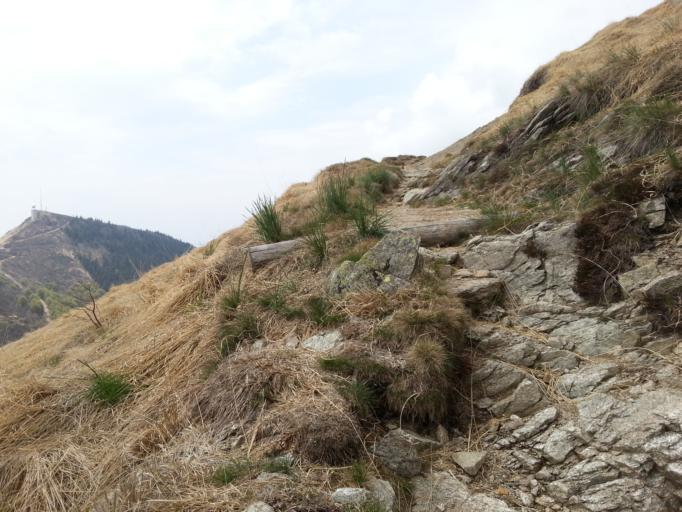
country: IT
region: Lombardy
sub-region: Provincia di Varese
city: Curiglia
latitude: 46.0468
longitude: 8.8431
